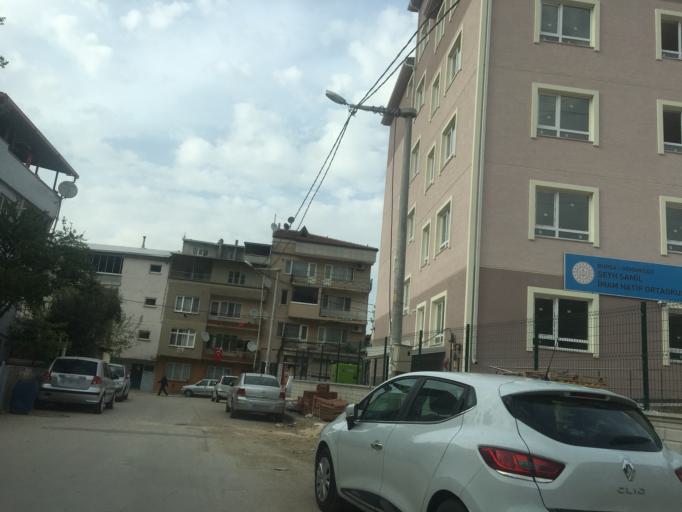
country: TR
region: Bursa
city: Yildirim
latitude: 40.2041
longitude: 29.0463
